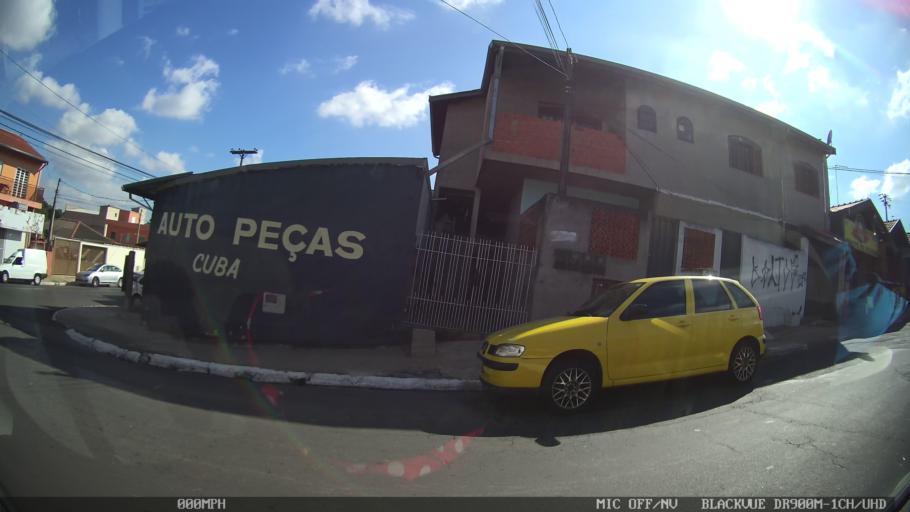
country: BR
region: Sao Paulo
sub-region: Hortolandia
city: Hortolandia
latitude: -22.8915
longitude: -47.1968
